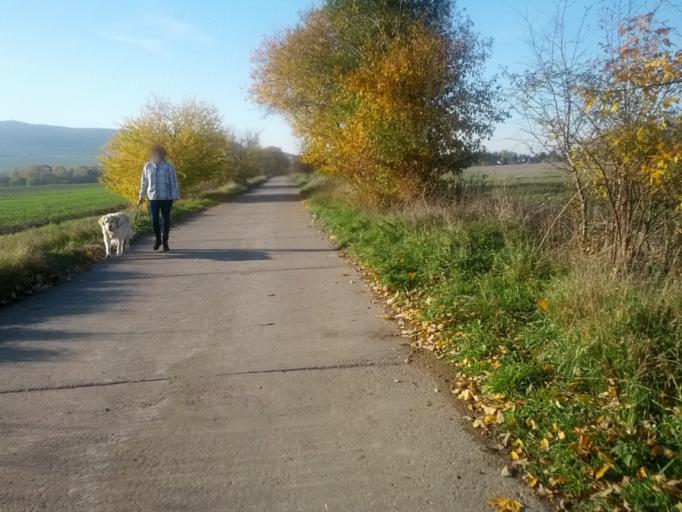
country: DE
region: Thuringia
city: Mechterstadt
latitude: 50.9510
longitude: 10.5073
